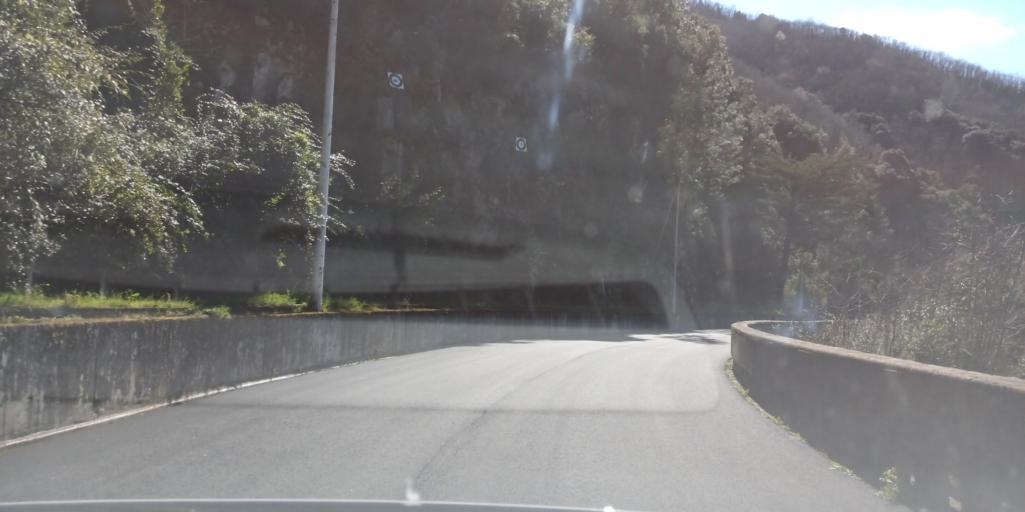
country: ES
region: Catalonia
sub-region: Provincia de Girona
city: Susqueda
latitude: 41.9790
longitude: 2.5297
